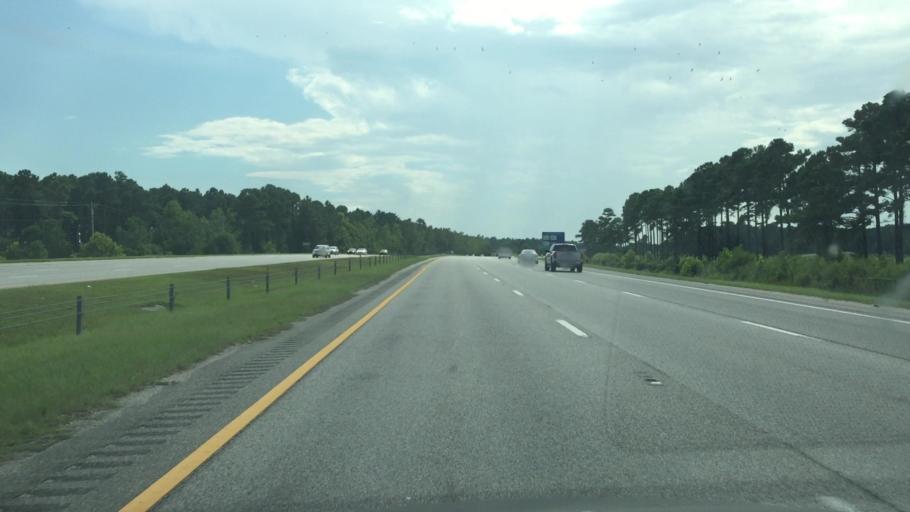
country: US
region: South Carolina
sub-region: Horry County
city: Myrtle Beach
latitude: 33.7593
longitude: -78.8422
